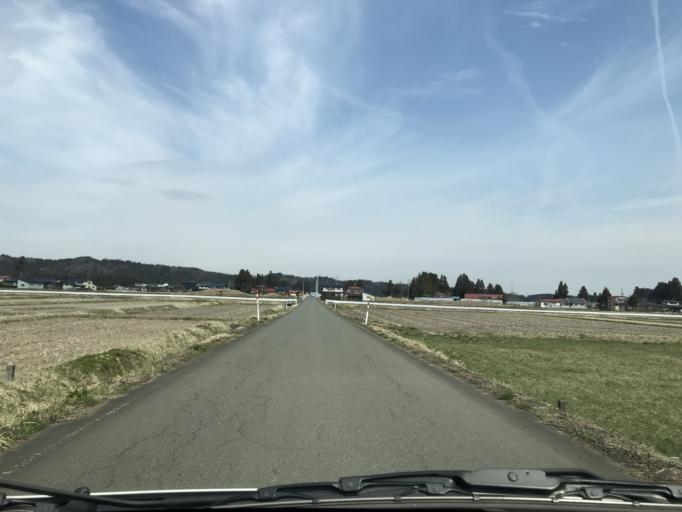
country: JP
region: Iwate
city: Mizusawa
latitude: 39.1323
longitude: 141.0482
